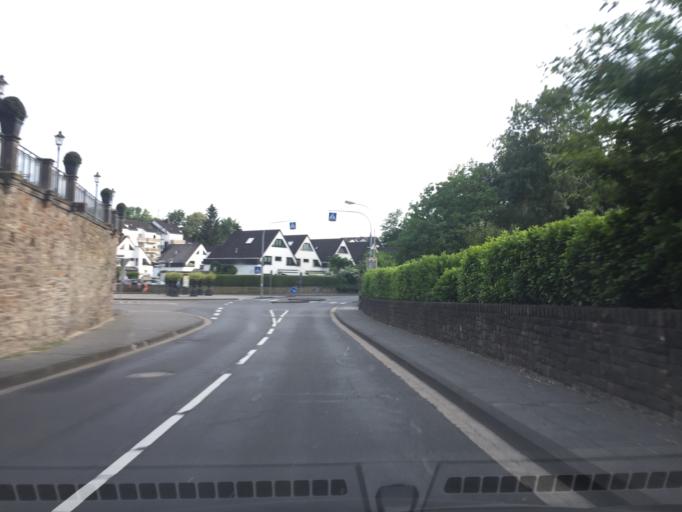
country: DE
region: Rheinland-Pfalz
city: Bendorf
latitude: 50.4388
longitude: 7.5767
